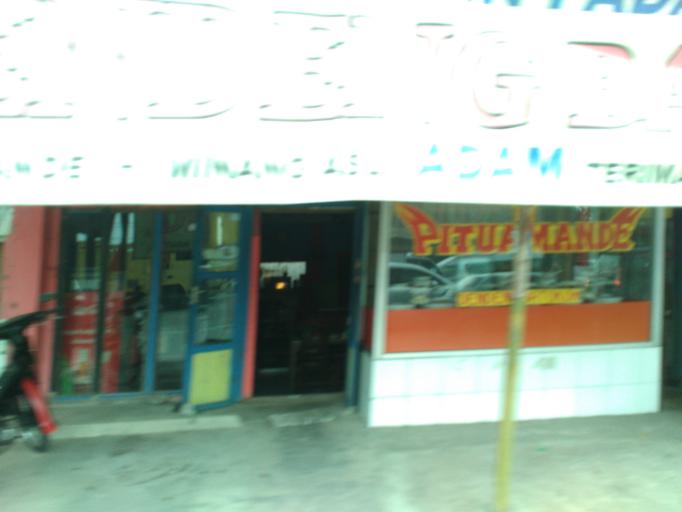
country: ID
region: Central Java
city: Gatak
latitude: -7.6060
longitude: 110.7023
